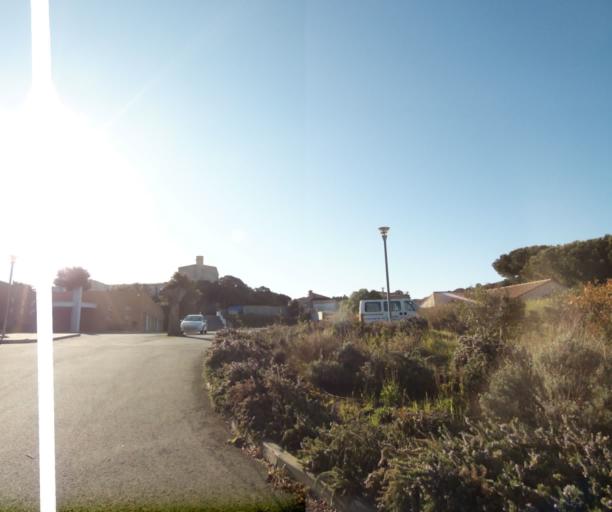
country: FR
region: Corsica
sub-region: Departement de la Corse-du-Sud
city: Propriano
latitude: 41.6714
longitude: 8.9143
